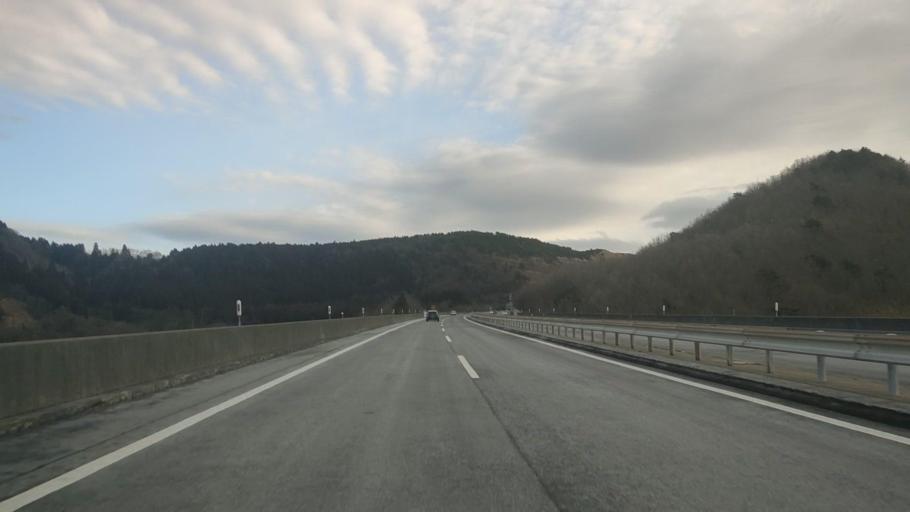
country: JP
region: Oita
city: Beppu
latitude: 33.2928
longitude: 131.3554
